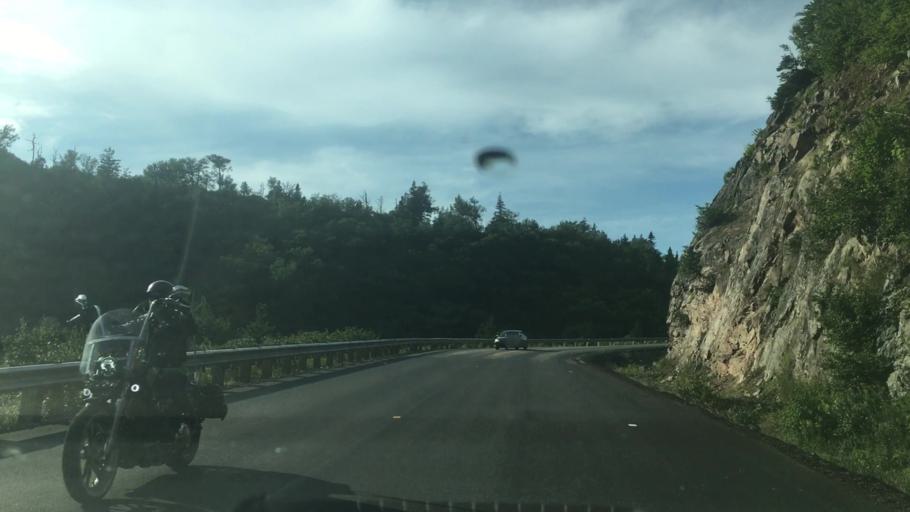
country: CA
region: Nova Scotia
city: Sydney Mines
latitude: 46.8206
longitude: -60.6536
